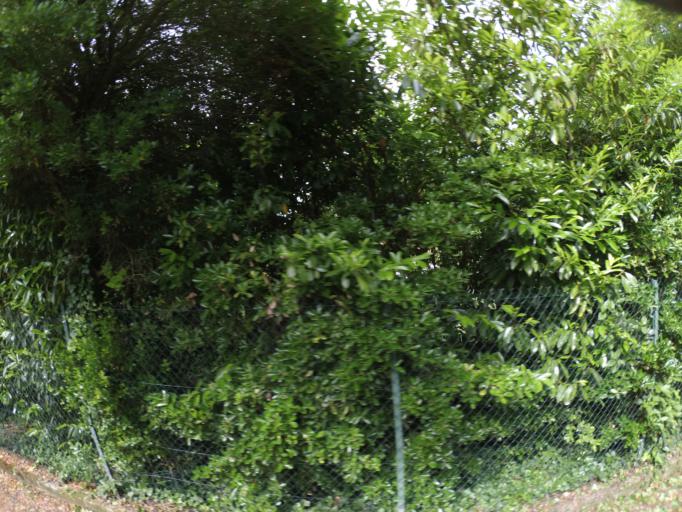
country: FR
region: Poitou-Charentes
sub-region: Departement de la Charente-Maritime
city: Angoulins
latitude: 46.0963
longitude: -1.1030
